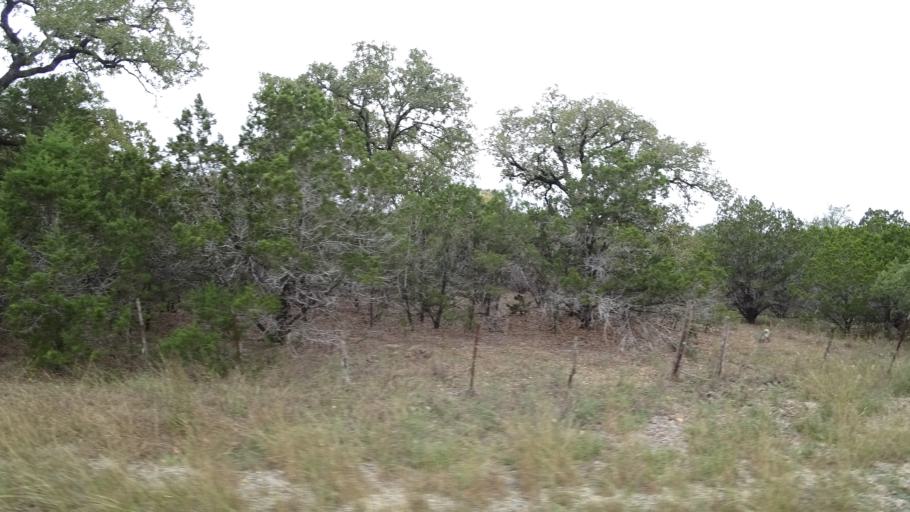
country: US
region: Texas
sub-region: Travis County
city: Bee Cave
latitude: 30.3443
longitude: -97.9329
